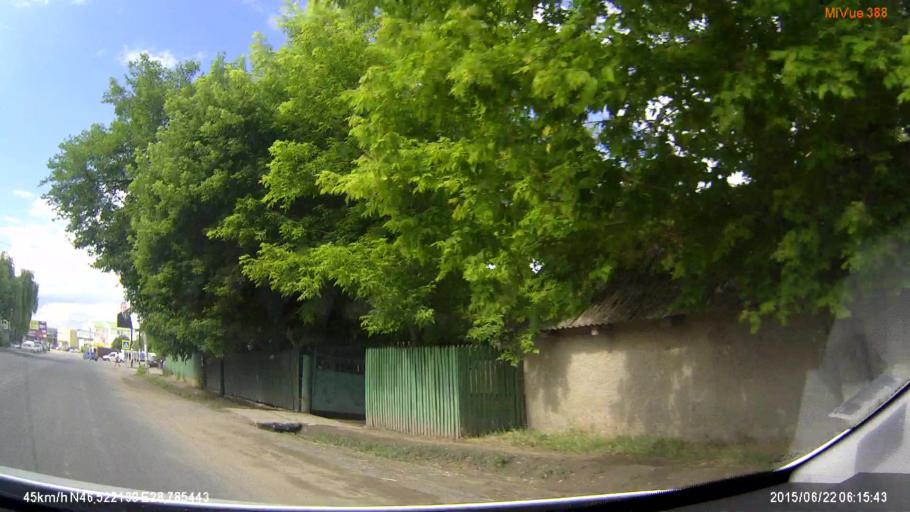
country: MD
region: Cimislia
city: Cimislia
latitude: 46.5219
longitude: 28.7855
